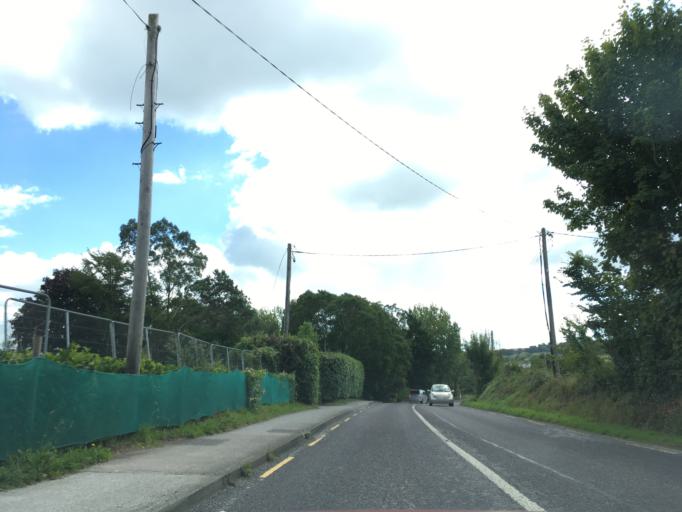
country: IE
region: Munster
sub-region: County Cork
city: Carrigaline
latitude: 51.8117
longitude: -8.3778
